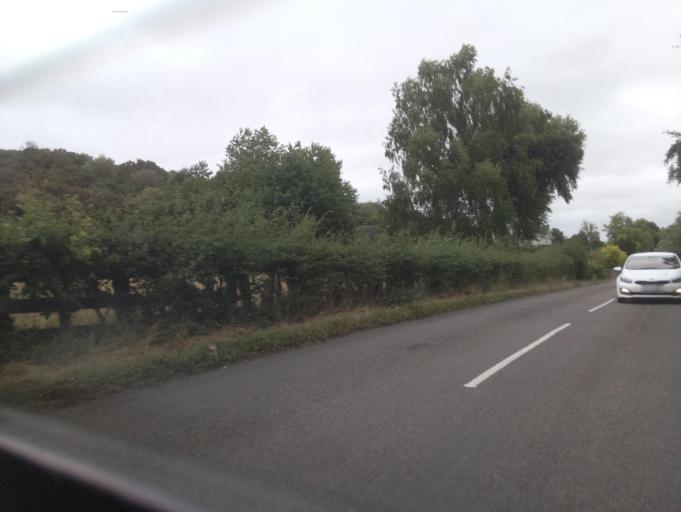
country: GB
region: England
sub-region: Derbyshire
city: Repton
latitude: 52.8147
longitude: -1.5444
